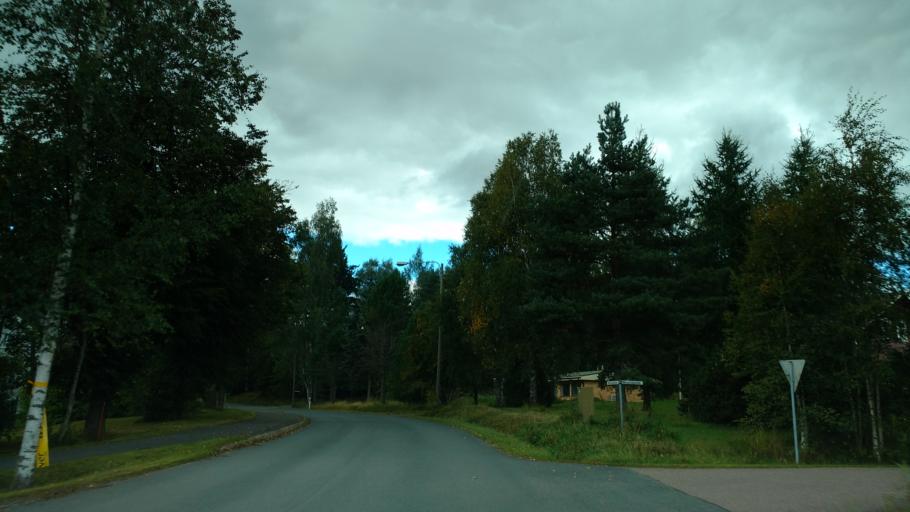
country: FI
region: Haeme
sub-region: Forssa
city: Ypaejae
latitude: 60.8057
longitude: 23.2724
